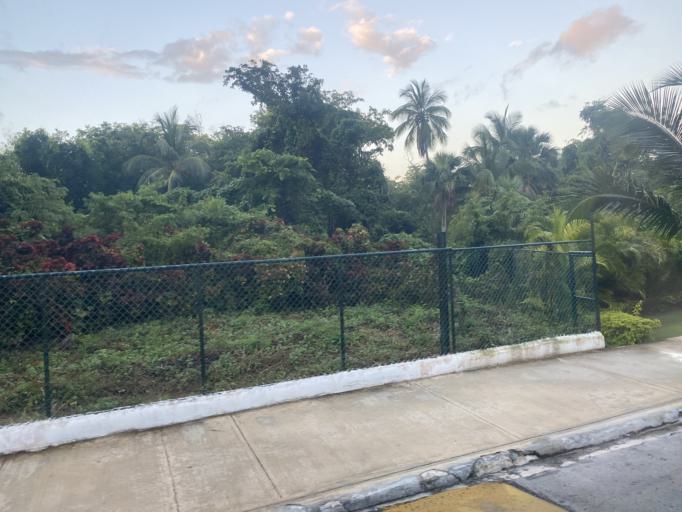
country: DO
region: San Juan
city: Punta Cana
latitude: 18.7214
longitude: -68.4592
